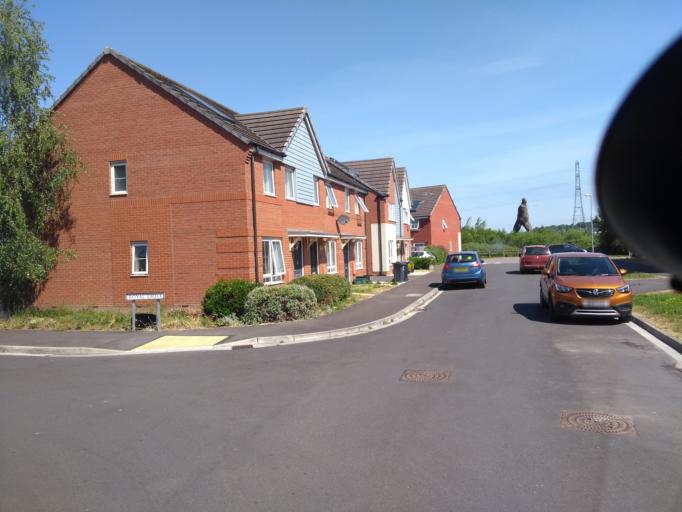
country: GB
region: England
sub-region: Somerset
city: Puriton
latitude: 51.1494
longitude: -2.9814
